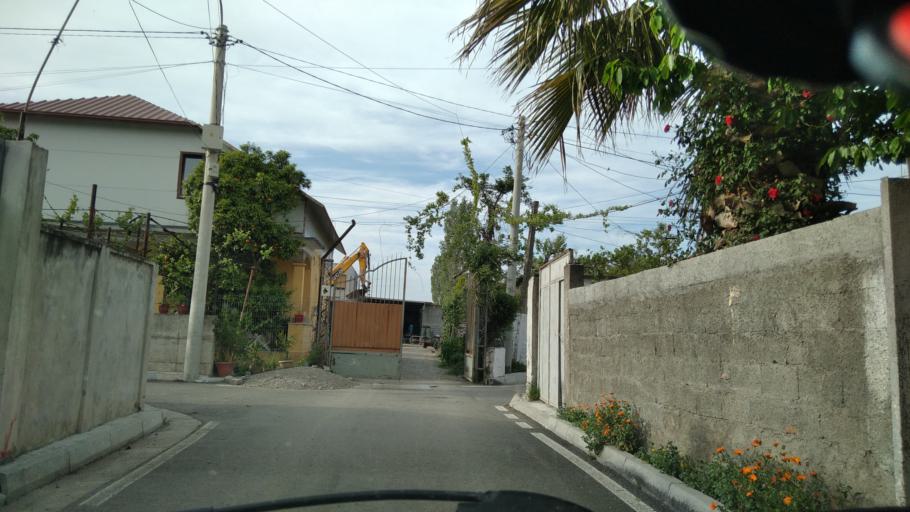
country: AL
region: Shkoder
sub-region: Rrethi i Shkodres
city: Shkoder
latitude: 42.0803
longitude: 19.5012
